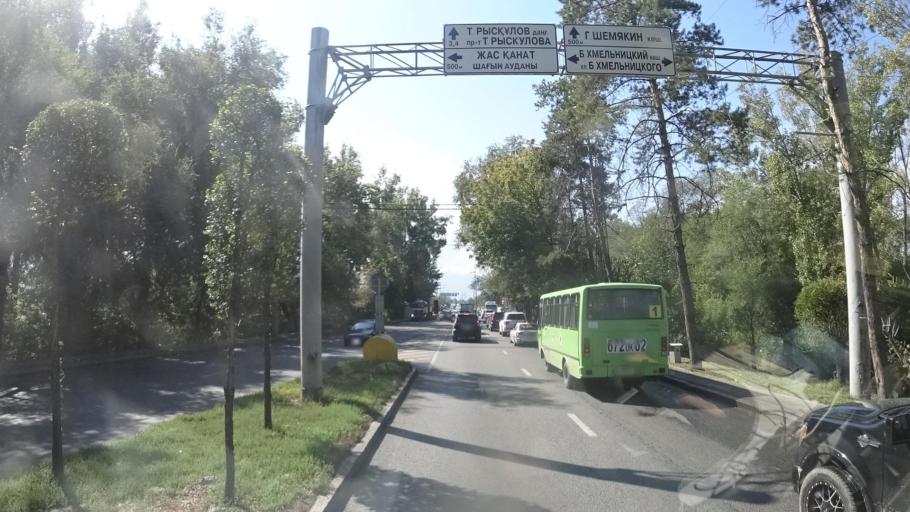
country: KZ
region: Almaty Oblysy
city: Pervomayskiy
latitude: 43.3228
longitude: 76.9733
